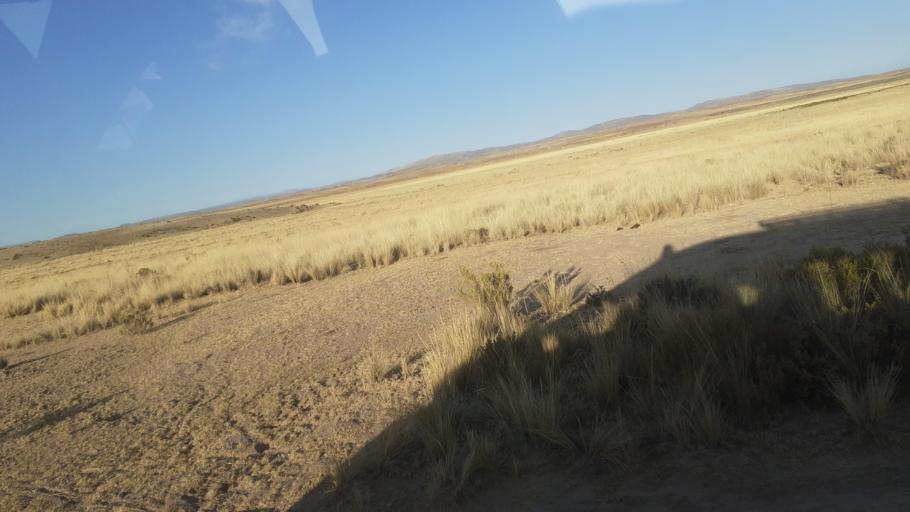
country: BO
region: La Paz
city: Tiahuanaco
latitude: -16.9479
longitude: -68.7621
